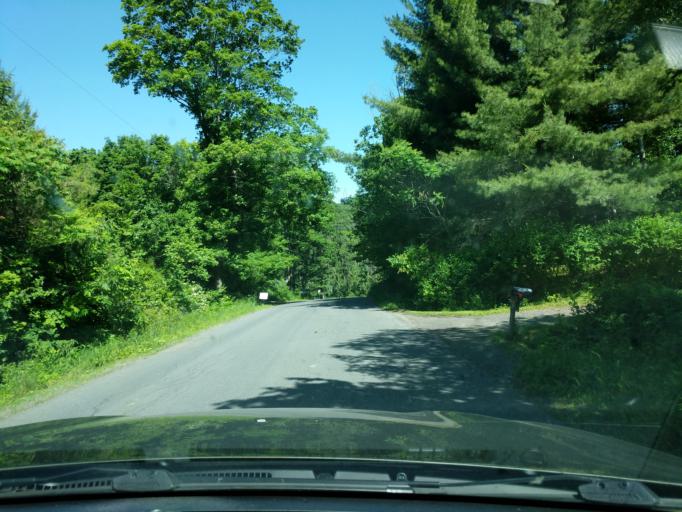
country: US
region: New York
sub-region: Tompkins County
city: East Ithaca
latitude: 42.3817
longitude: -76.3806
